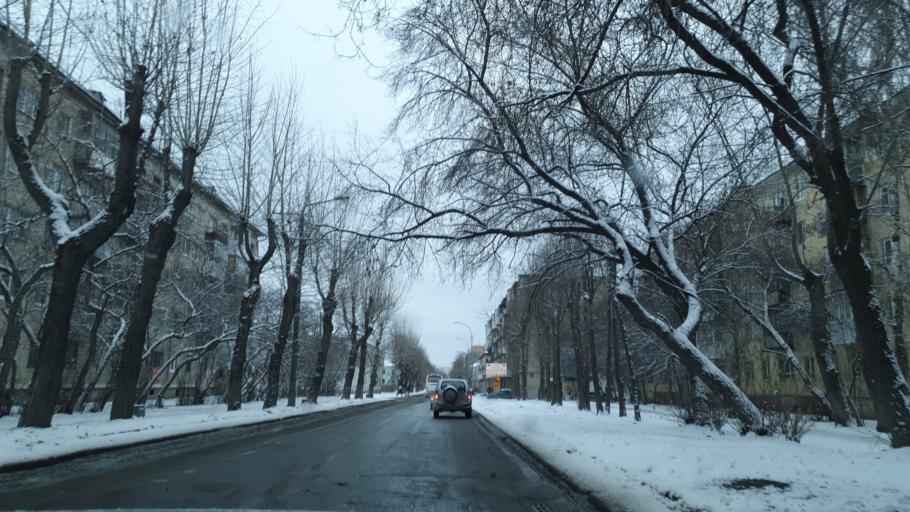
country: RU
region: Sverdlovsk
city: Istok
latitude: 56.7516
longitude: 60.7090
